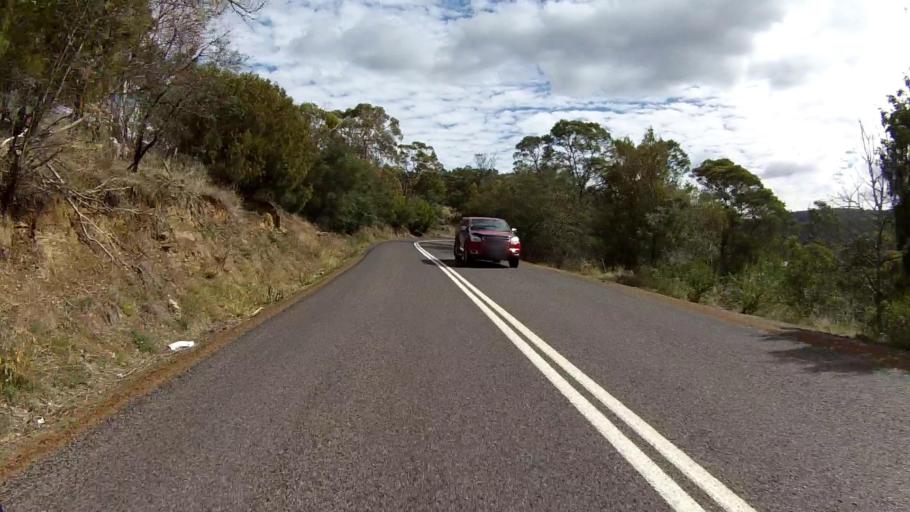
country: AU
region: Tasmania
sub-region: Clarence
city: Lindisfarne
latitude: -42.8059
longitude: 147.3543
